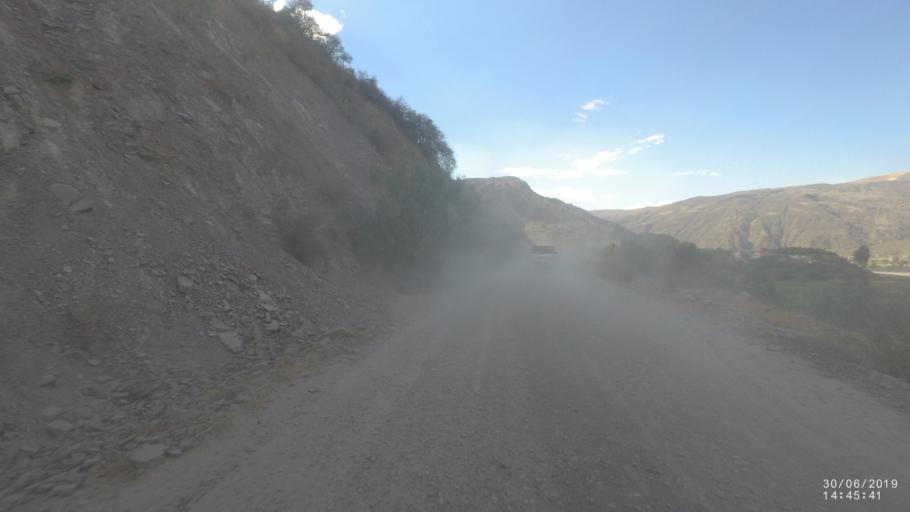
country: BO
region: Cochabamba
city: Irpa Irpa
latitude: -17.7975
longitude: -66.3505
